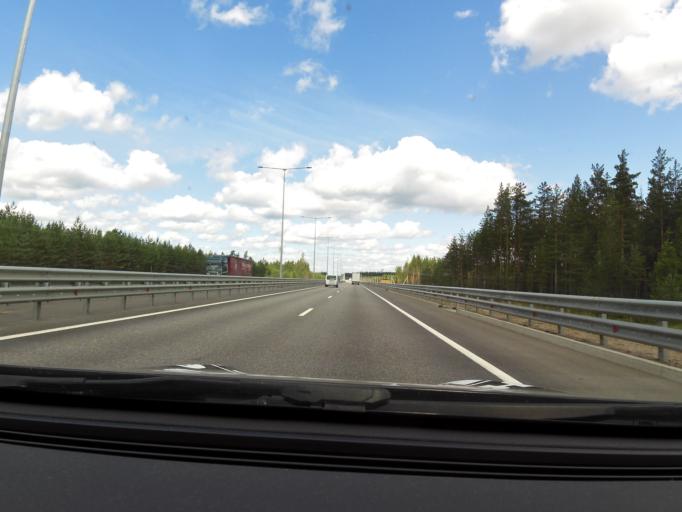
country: RU
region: Tverskaya
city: Krasnomayskiy
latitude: 57.5439
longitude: 34.2713
